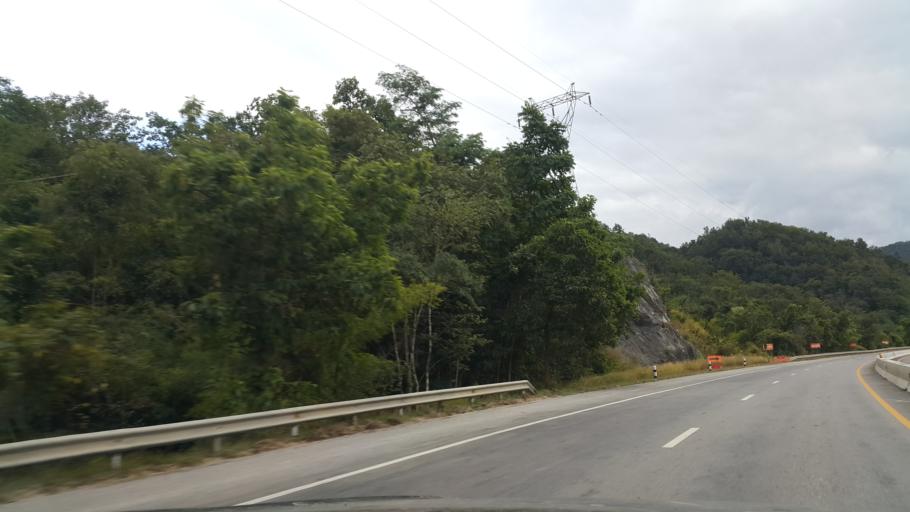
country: TH
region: Lampang
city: Sop Prap
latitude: 17.8408
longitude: 99.2935
